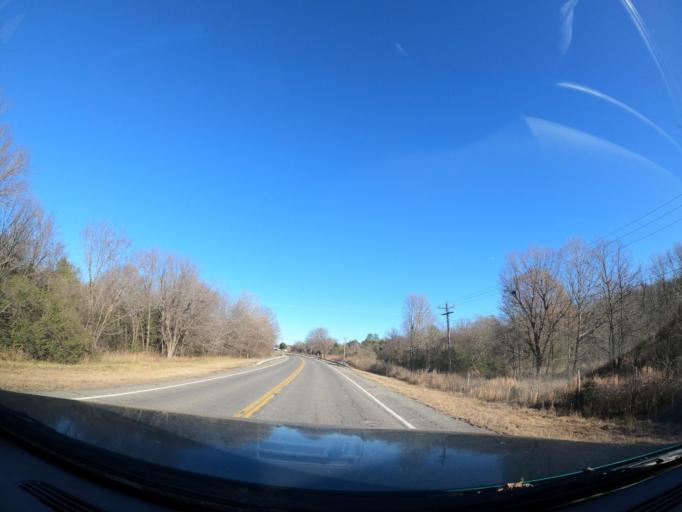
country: US
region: Oklahoma
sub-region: Pittsburg County
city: Quinton
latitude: 35.2143
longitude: -95.4147
